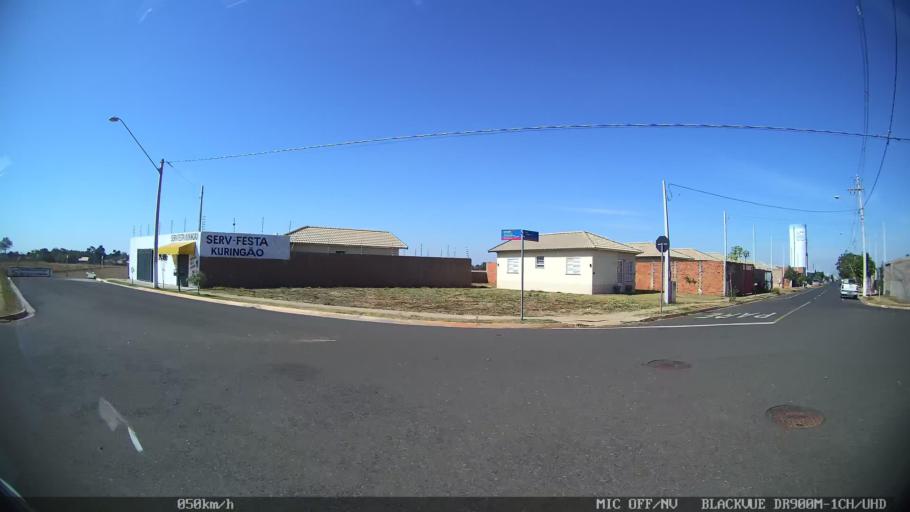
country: BR
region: Sao Paulo
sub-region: Sao Jose Do Rio Preto
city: Sao Jose do Rio Preto
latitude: -20.7469
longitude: -49.4358
